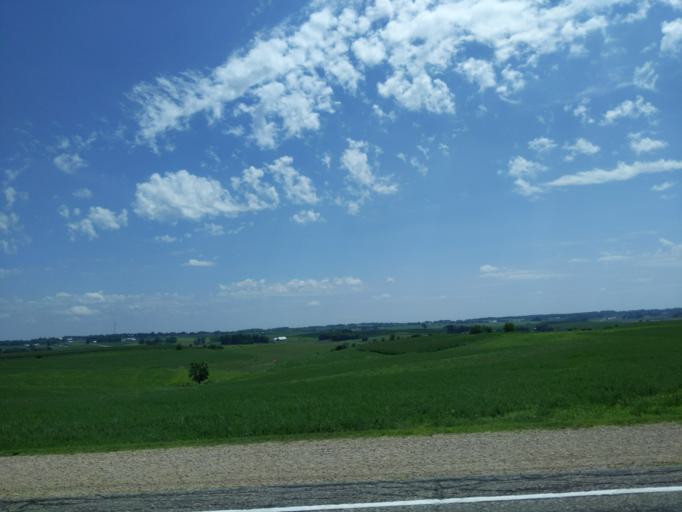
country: US
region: Wisconsin
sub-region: Vernon County
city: Westby
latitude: 43.6607
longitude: -90.9019
